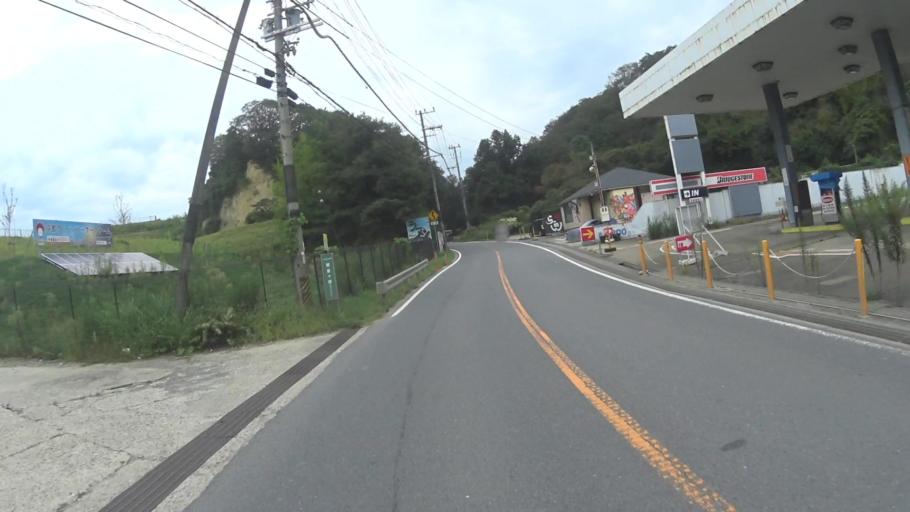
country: JP
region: Kyoto
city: Uji
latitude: 34.8391
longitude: 135.8314
